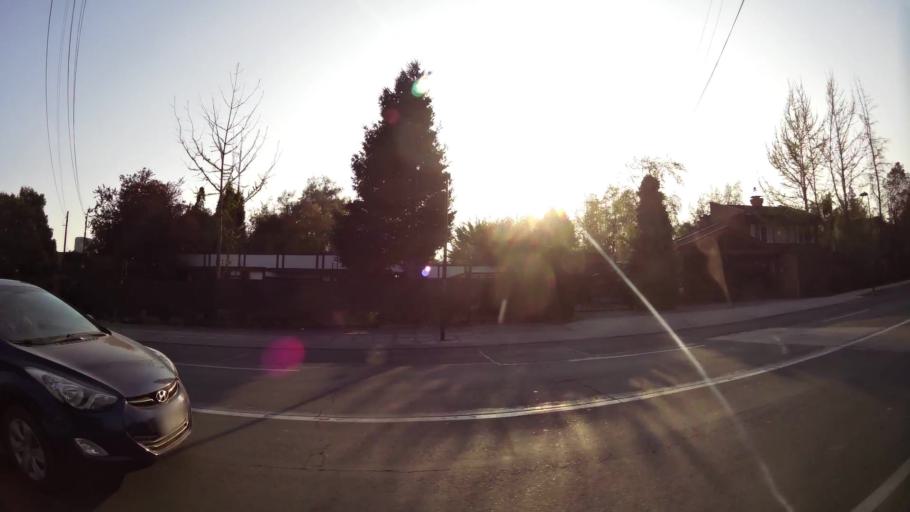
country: CL
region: Santiago Metropolitan
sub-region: Provincia de Santiago
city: Villa Presidente Frei, Nunoa, Santiago, Chile
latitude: -33.3484
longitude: -70.5105
